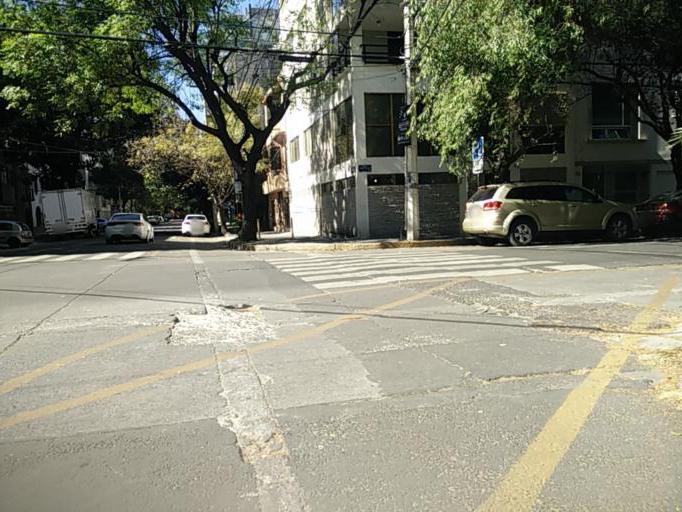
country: MX
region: Mexico City
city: Benito Juarez
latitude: 19.4085
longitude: -99.1738
